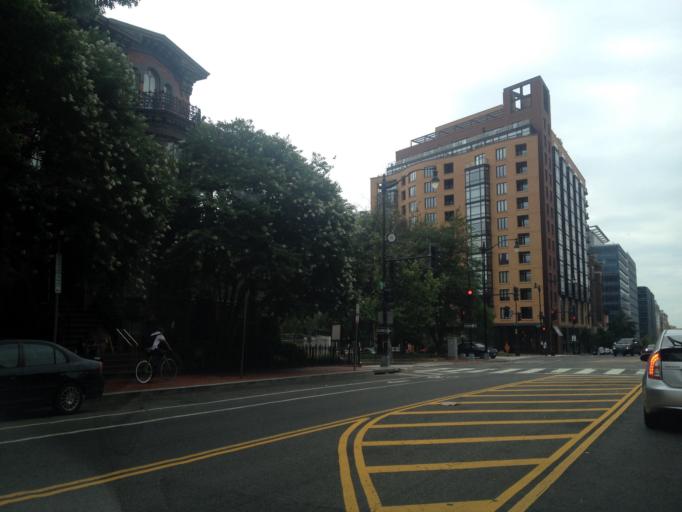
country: US
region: Washington, D.C.
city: Washington, D.C.
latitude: 38.9045
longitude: -77.0271
